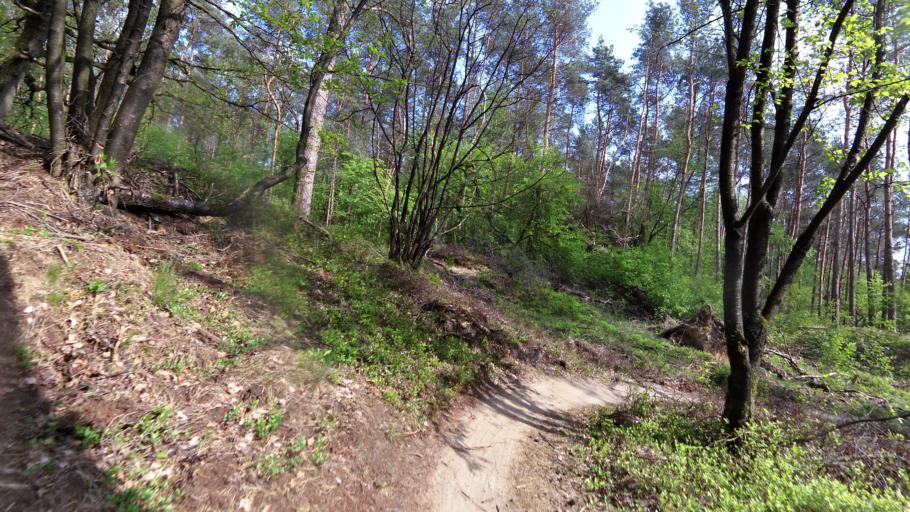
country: NL
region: Gelderland
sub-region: Gemeente Renkum
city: Wolfheze
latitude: 52.0333
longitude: 5.7615
